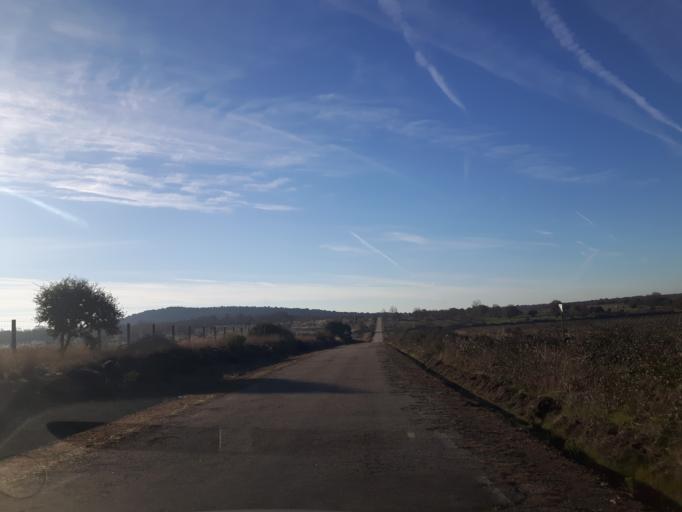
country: ES
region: Castille and Leon
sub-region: Provincia de Salamanca
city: Olmedo de Camaces
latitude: 40.9188
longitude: -6.6166
